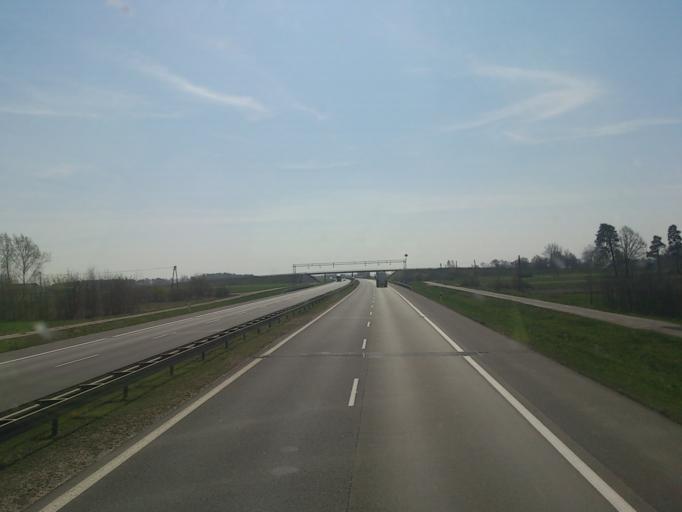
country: PL
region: Lodz Voivodeship
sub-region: Powiat piotrkowski
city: Grabica
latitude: 51.5135
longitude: 19.6010
